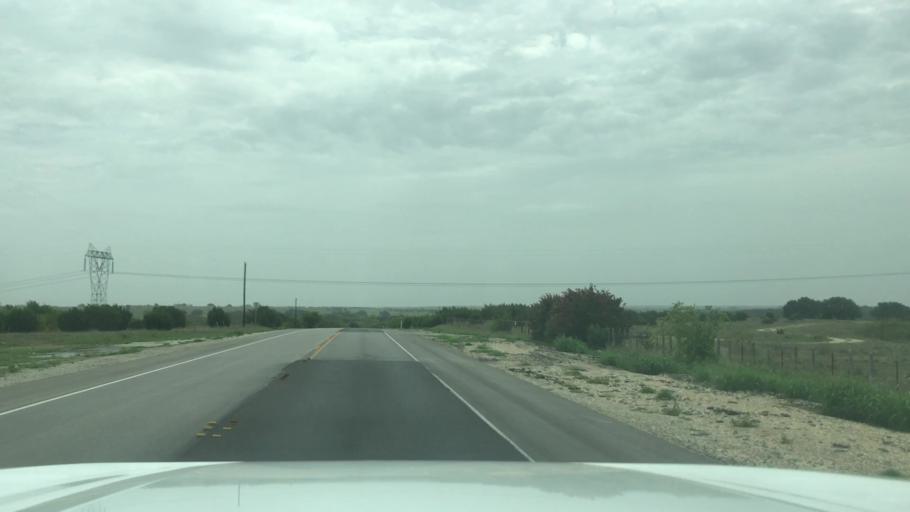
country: US
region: Texas
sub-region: Erath County
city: Dublin
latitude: 32.0772
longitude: -98.2376
